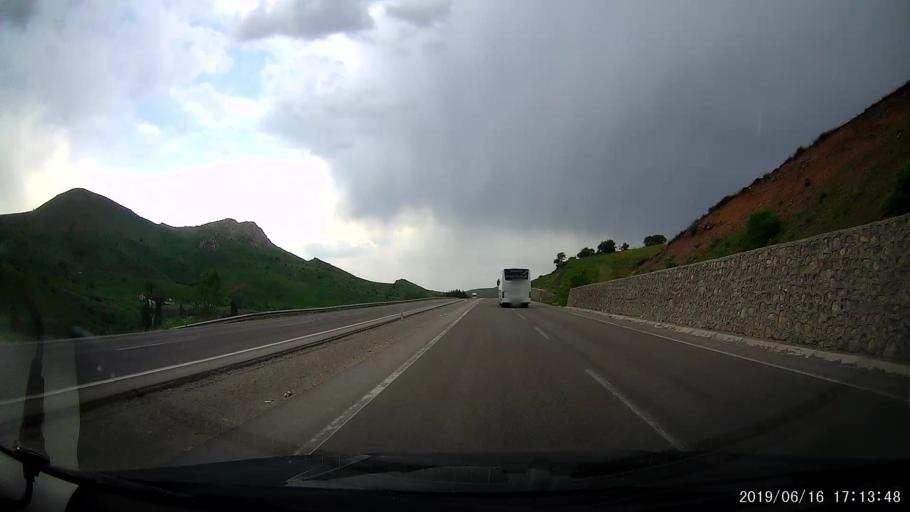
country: TR
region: Erzurum
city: Askale
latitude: 39.8563
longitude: 40.5901
